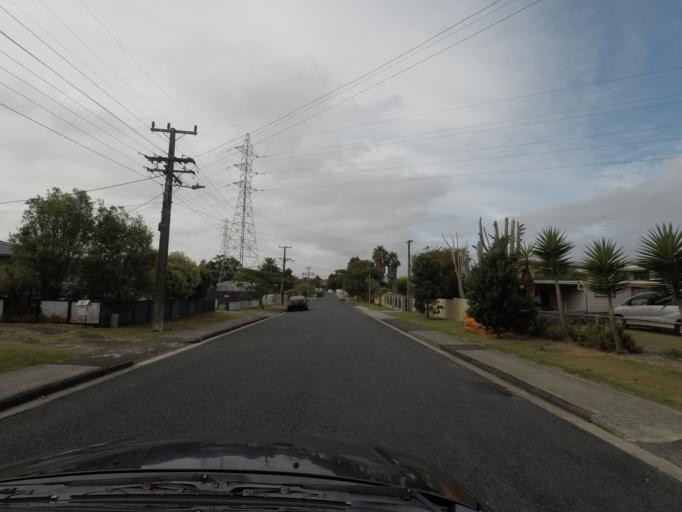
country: NZ
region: Auckland
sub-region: Auckland
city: Rosebank
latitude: -36.8929
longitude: 174.6660
